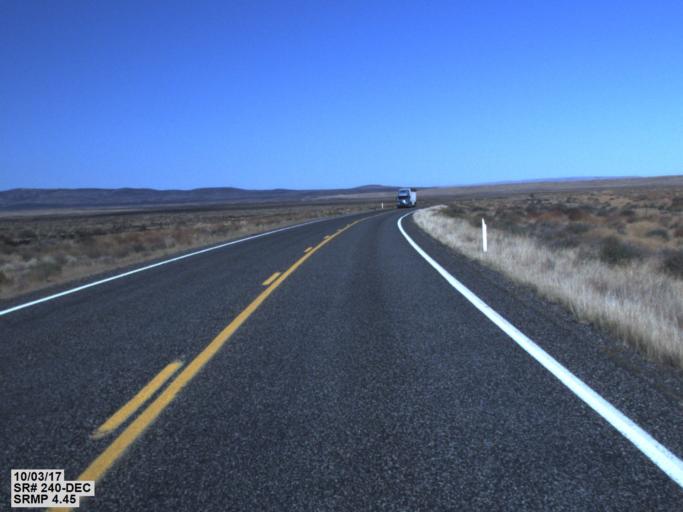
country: US
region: Washington
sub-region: Grant County
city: Desert Aire
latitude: 46.5256
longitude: -119.6785
